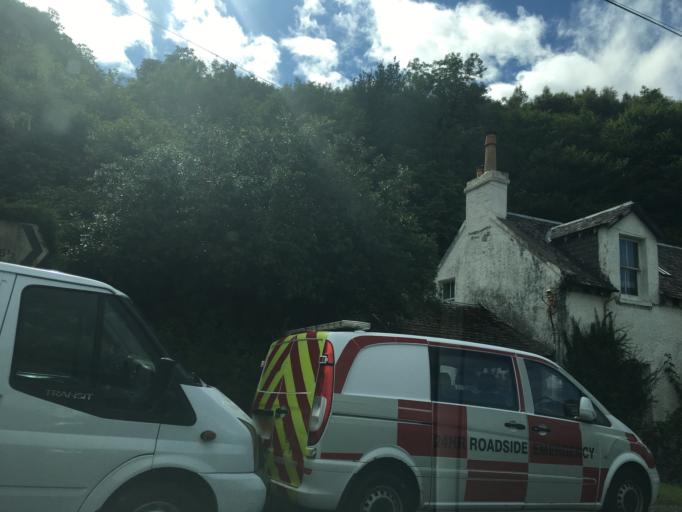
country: GB
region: Scotland
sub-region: Argyll and Bute
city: Ardrishaig
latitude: 56.0735
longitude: -5.5299
